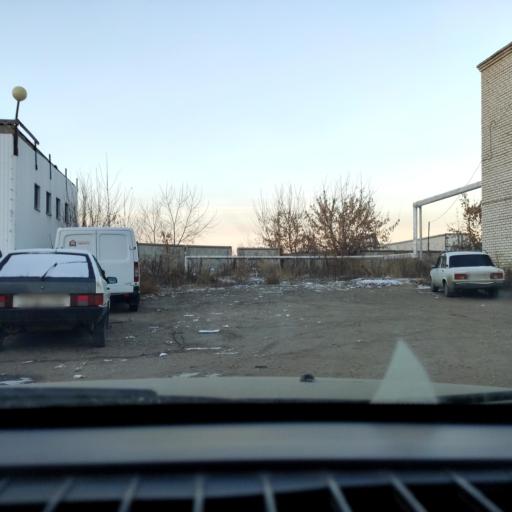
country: RU
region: Samara
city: Tol'yatti
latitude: 53.5405
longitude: 49.2904
